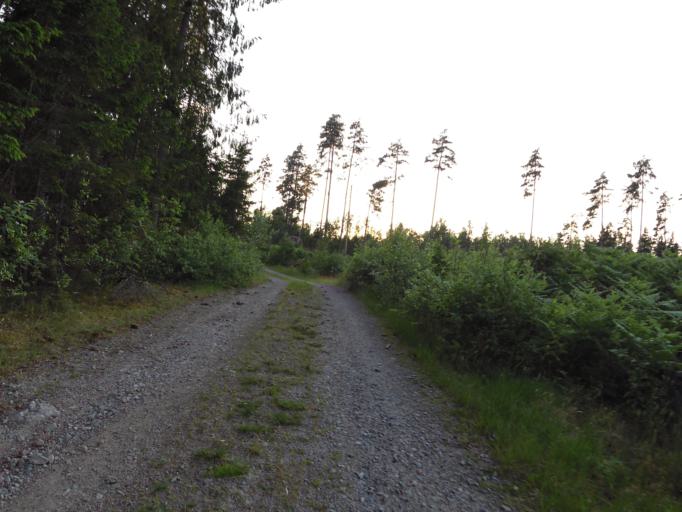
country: SE
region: Blekinge
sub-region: Olofstroms Kommun
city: Olofstroem
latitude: 56.4059
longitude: 14.5449
